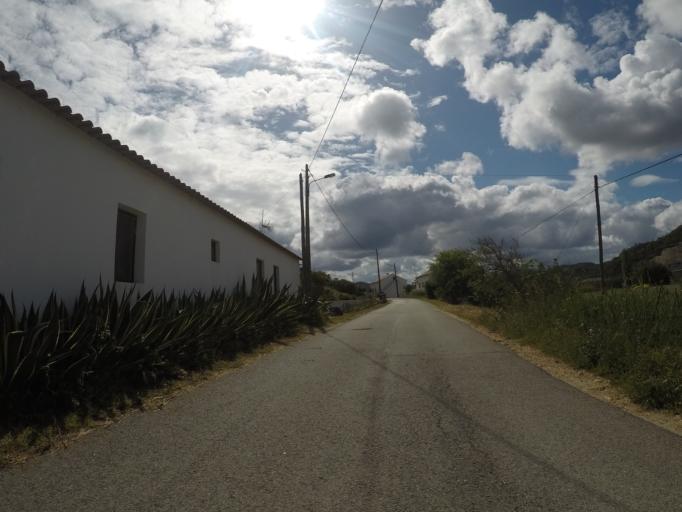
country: PT
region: Beja
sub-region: Odemira
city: Sao Teotonio
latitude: 37.4367
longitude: -8.7680
